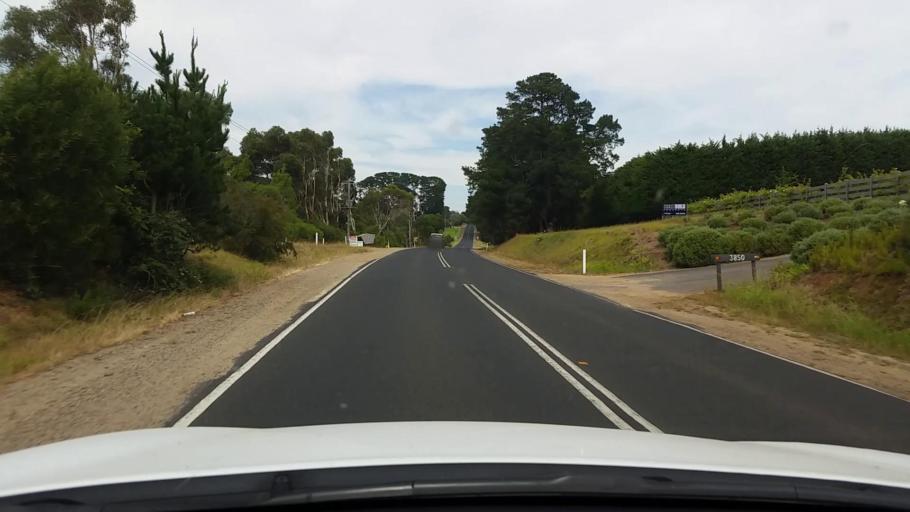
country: AU
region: Victoria
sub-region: Mornington Peninsula
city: Merricks
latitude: -38.4129
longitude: 145.0564
